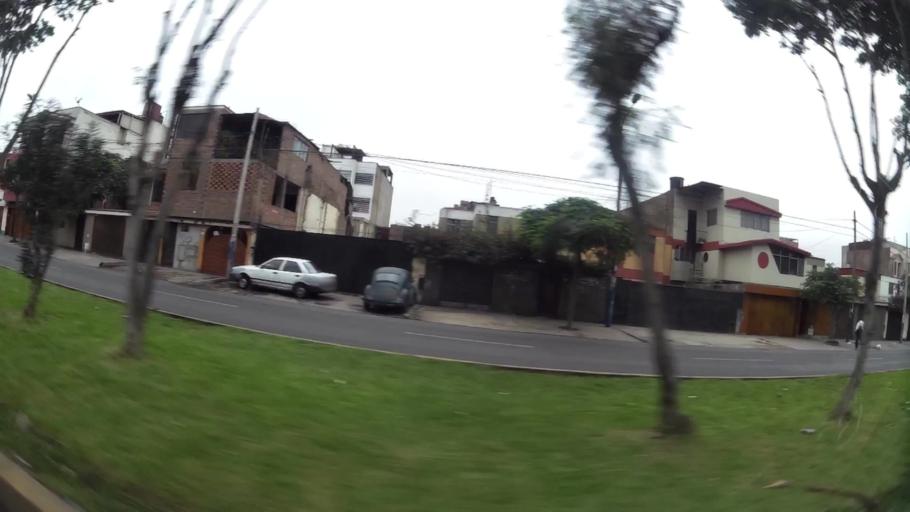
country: PE
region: Lima
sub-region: Lima
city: San Luis
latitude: -12.0738
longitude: -76.9823
